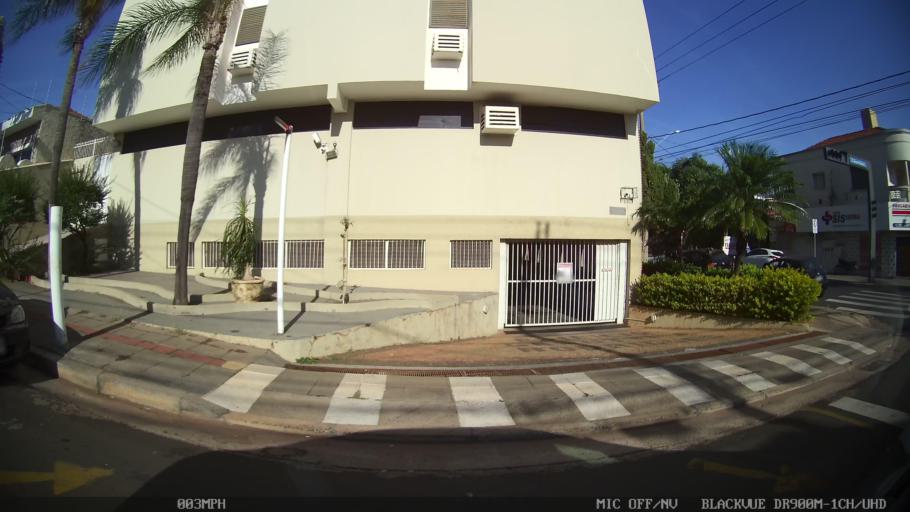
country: BR
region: Sao Paulo
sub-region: Sao Jose Do Rio Preto
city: Sao Jose do Rio Preto
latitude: -20.8024
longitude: -49.3725
